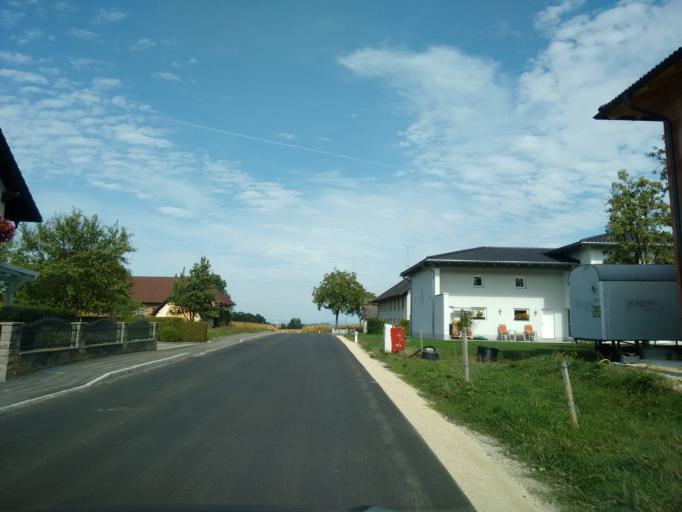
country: AT
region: Upper Austria
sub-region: Wels-Land
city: Marchtrenk
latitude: 48.1250
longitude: 14.0987
